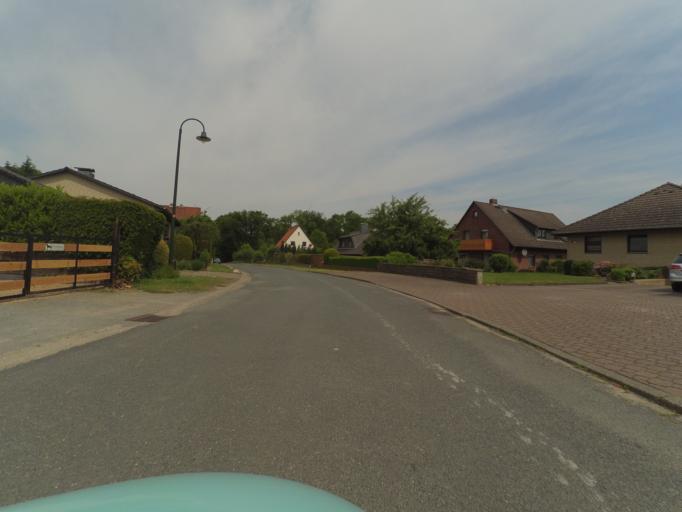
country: DE
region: Lower Saxony
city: Ilsede
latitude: 52.2713
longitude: 10.1432
